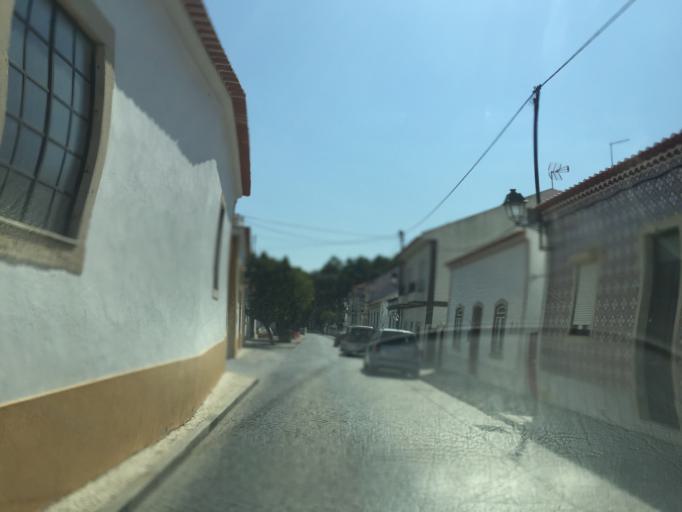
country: PT
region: Santarem
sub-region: Chamusca
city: Vila Nova da Barquinha
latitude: 39.4590
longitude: -8.4348
